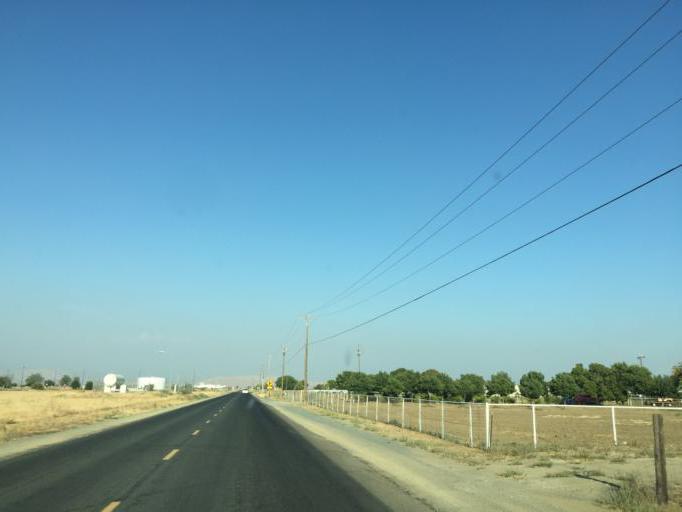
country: US
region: California
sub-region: Tulare County
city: Cutler
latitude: 36.4580
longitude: -119.3262
